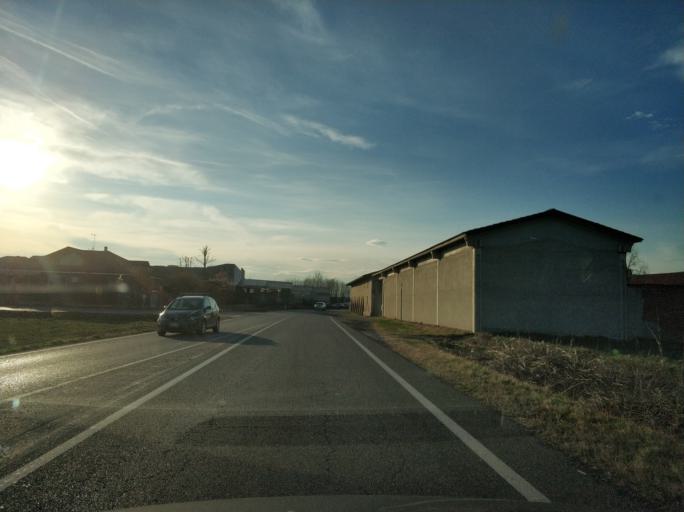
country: IT
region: Piedmont
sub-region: Provincia di Torino
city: Brandizzo
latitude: 45.1897
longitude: 7.8127
